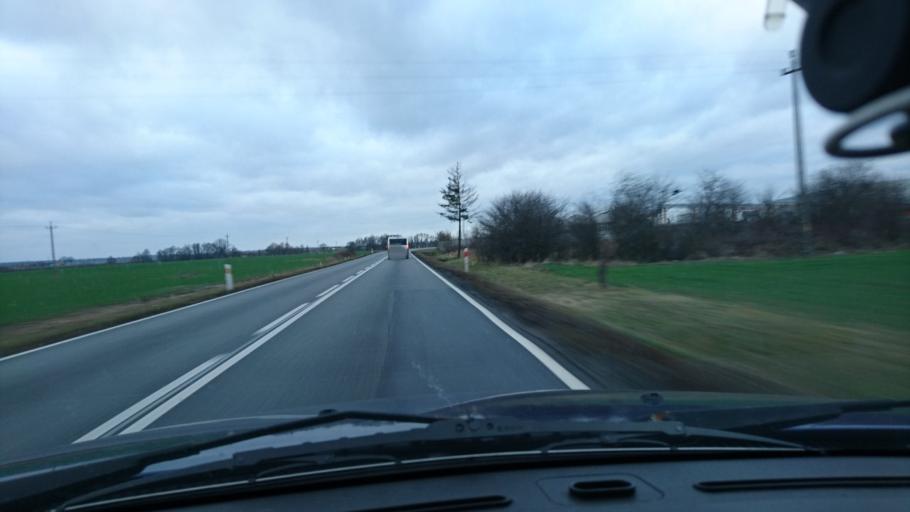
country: PL
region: Opole Voivodeship
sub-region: Powiat kluczborski
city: Kluczbork
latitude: 51.0009
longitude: 18.2059
